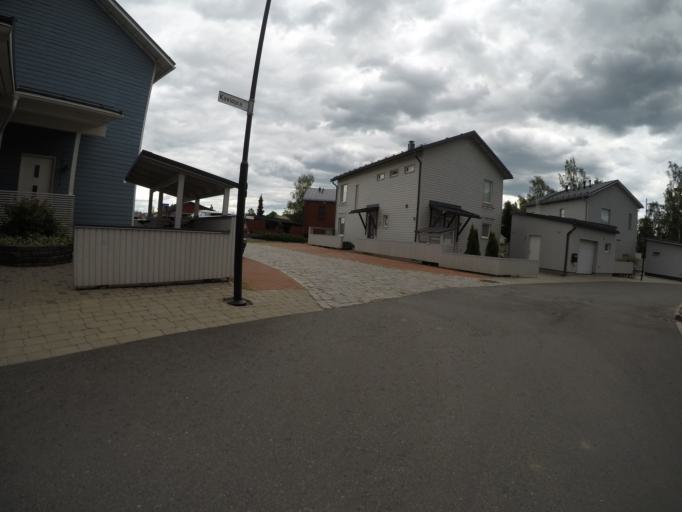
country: FI
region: Haeme
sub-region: Haemeenlinna
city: Haemeenlinna
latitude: 60.9911
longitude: 24.4314
